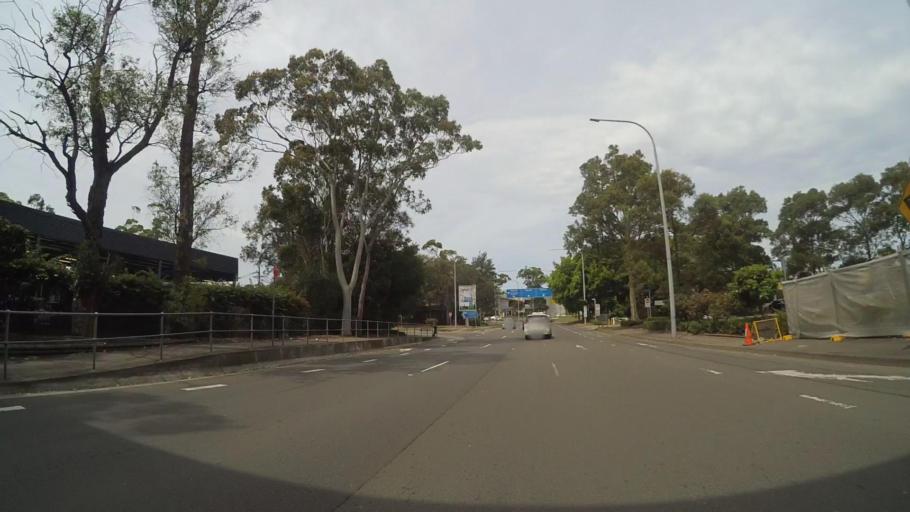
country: AU
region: New South Wales
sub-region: Botany Bay
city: Mascot
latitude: -33.9336
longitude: 151.1843
